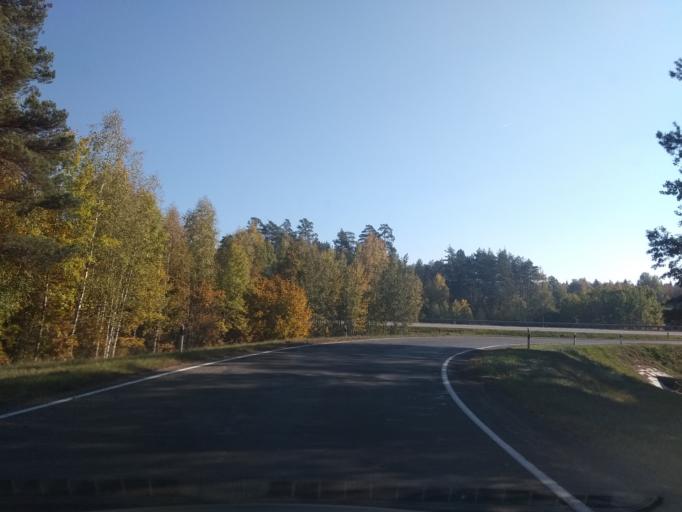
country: BY
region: Brest
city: Ivatsevichy
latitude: 52.8565
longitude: 25.6452
